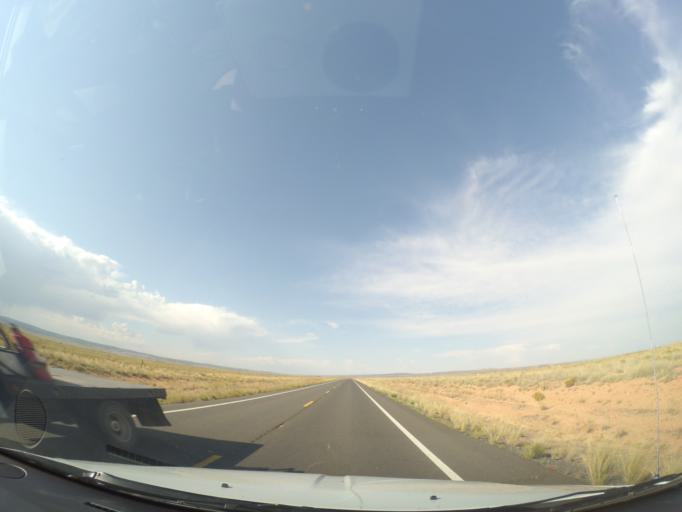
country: US
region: Arizona
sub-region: Coconino County
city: Tuba City
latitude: 36.3845
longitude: -111.4192
